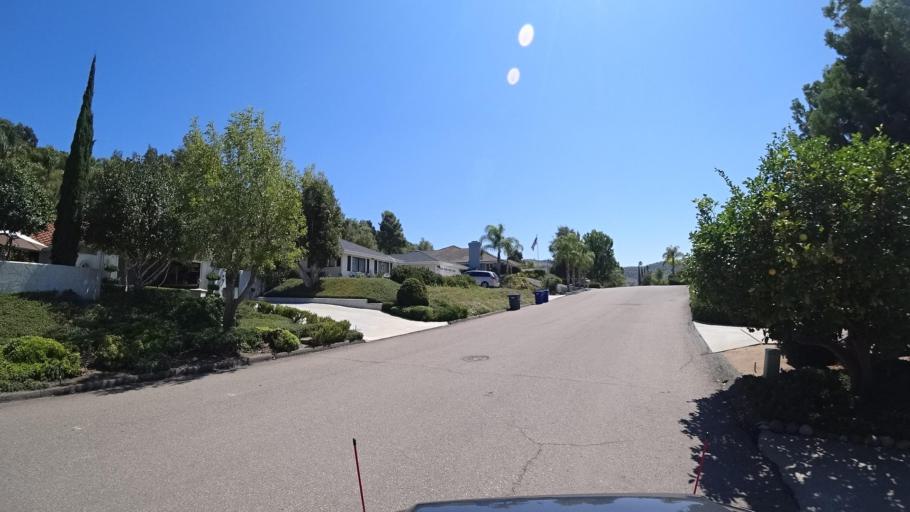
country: US
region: California
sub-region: San Diego County
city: Bonsall
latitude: 33.3401
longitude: -117.1842
